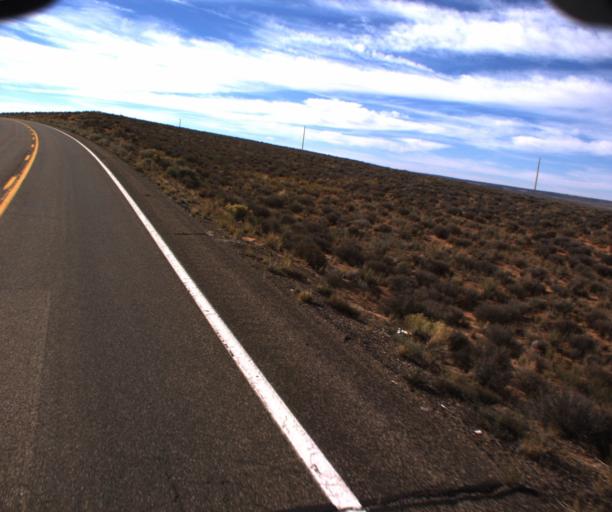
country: US
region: Arizona
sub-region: Coconino County
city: LeChee
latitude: 36.8073
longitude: -111.3065
